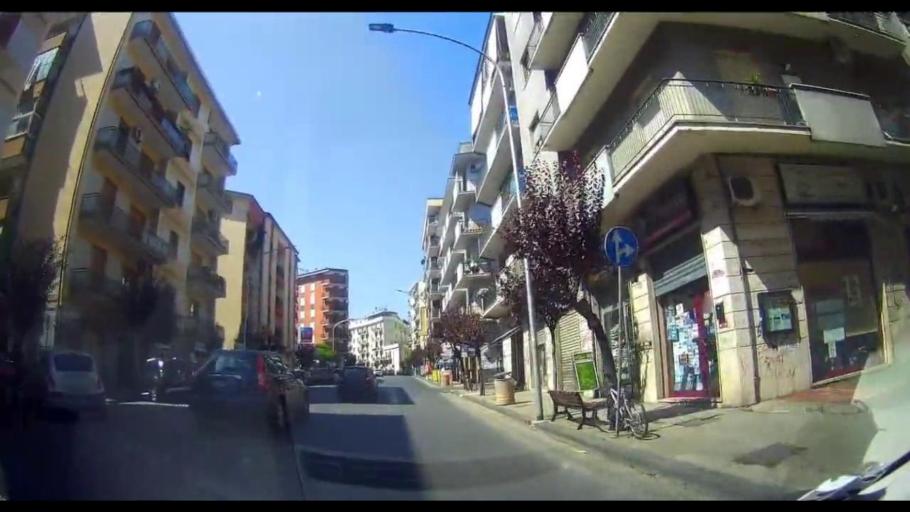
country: IT
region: Calabria
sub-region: Provincia di Cosenza
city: Cosenza
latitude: 39.3077
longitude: 16.2514
